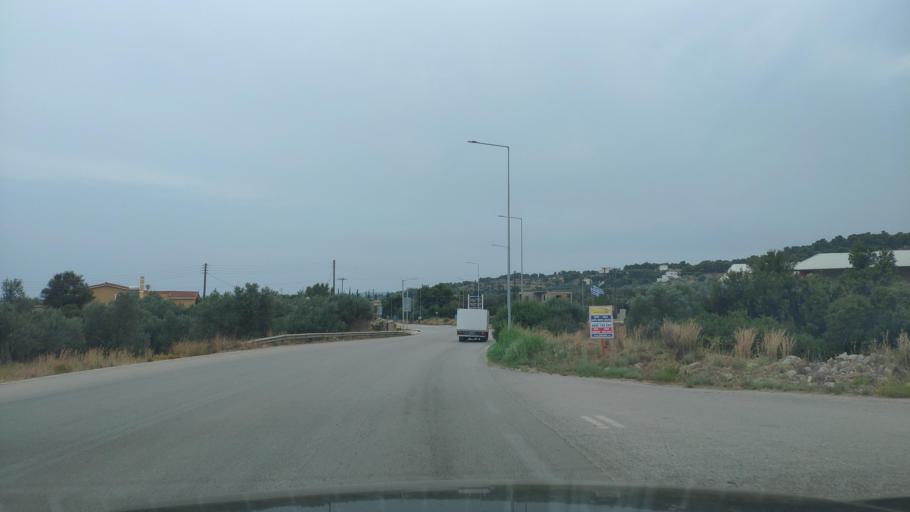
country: GR
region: Peloponnese
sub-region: Nomos Argolidos
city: Kranidi
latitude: 37.3524
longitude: 23.1579
